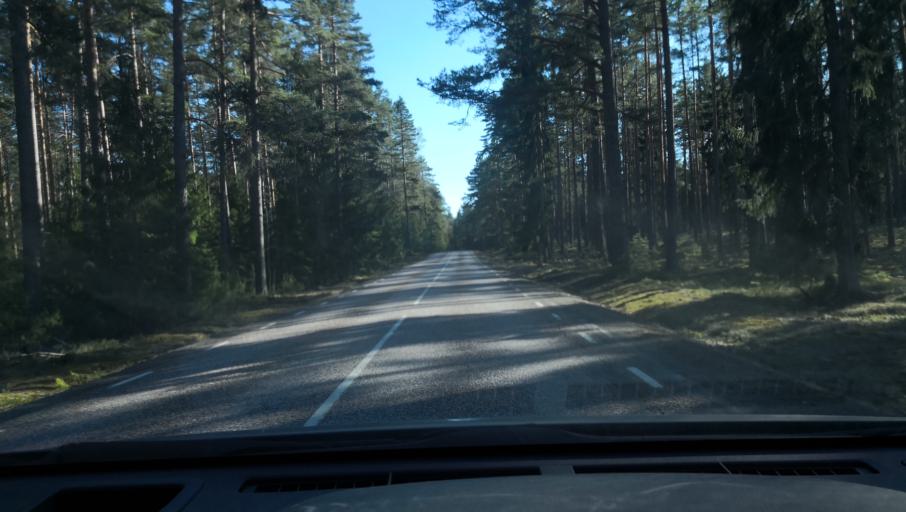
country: SE
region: Dalarna
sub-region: Avesta Kommun
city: Avesta
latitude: 59.9782
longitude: 16.3364
